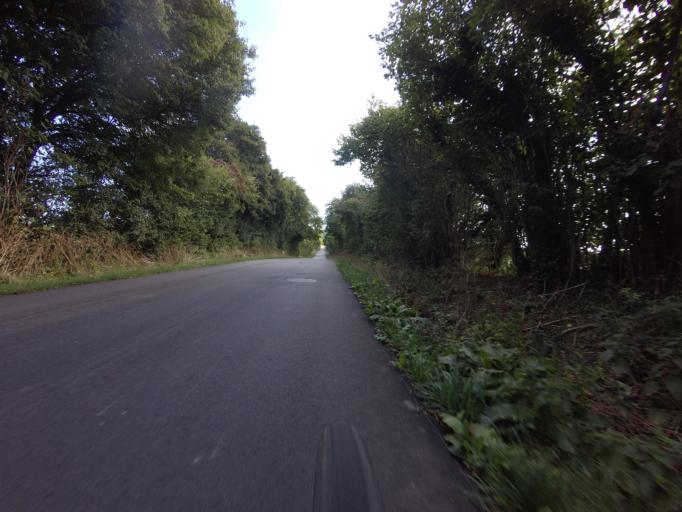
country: DK
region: Zealand
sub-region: Vordingborg Kommune
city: Stege
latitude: 54.9703
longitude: 12.4835
